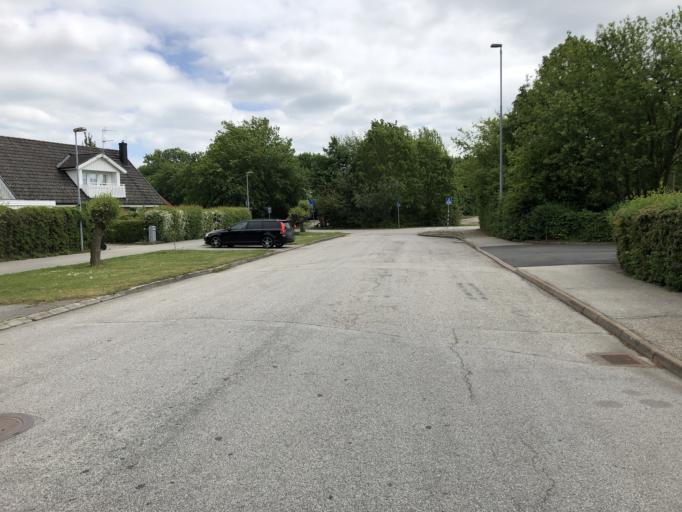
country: SE
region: Skane
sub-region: Lunds Kommun
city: Lund
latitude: 55.7064
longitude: 13.1632
